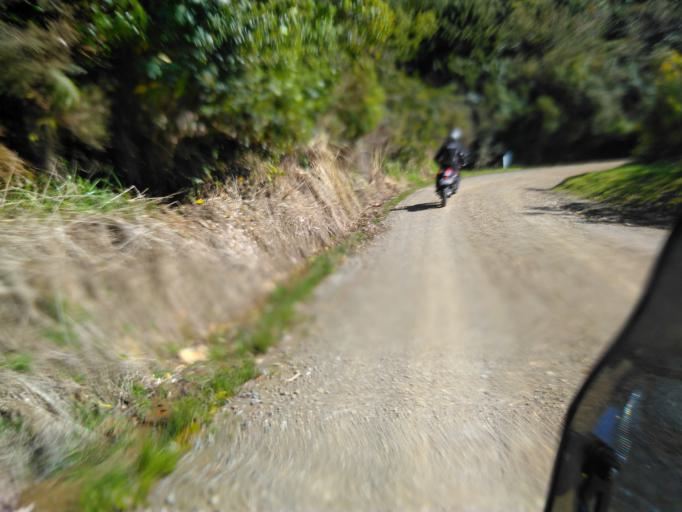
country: NZ
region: Bay of Plenty
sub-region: Opotiki District
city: Opotiki
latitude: -38.3394
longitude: 177.5811
